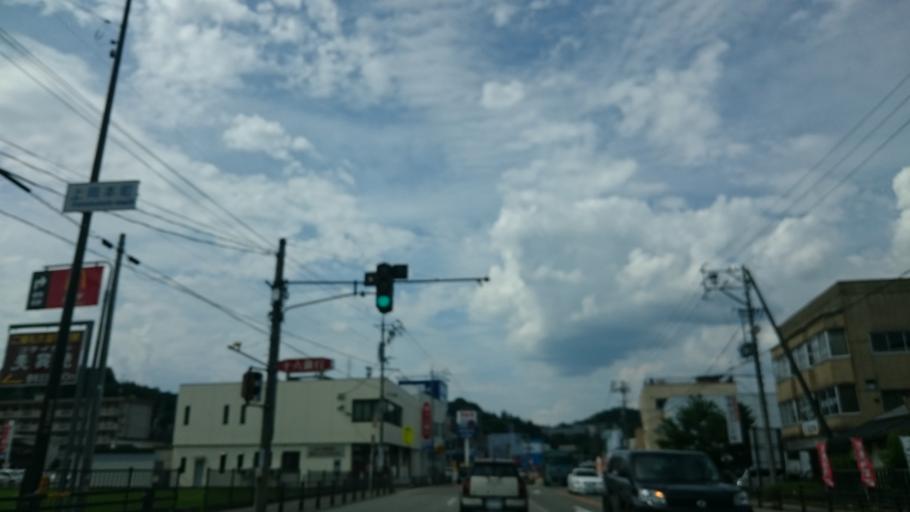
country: JP
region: Gifu
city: Takayama
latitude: 36.1403
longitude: 137.2432
